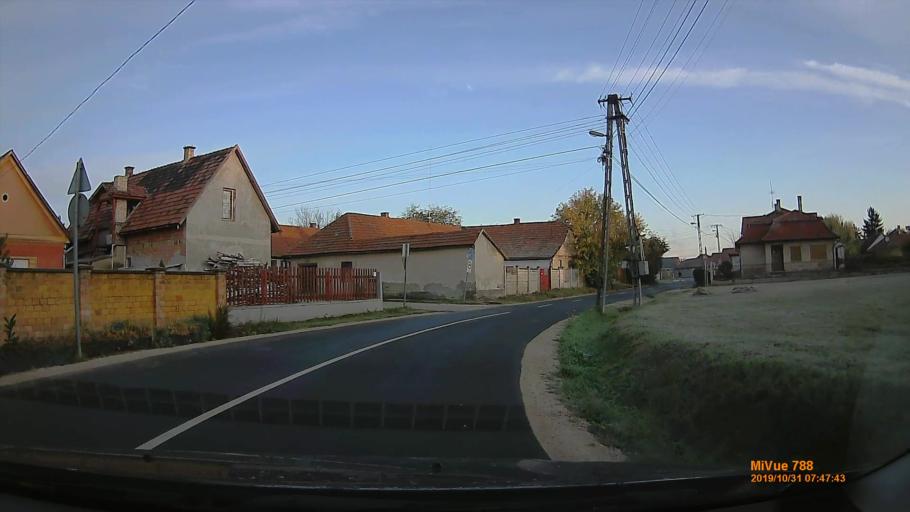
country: HU
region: Pest
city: Pilis
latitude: 47.2886
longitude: 19.5501
